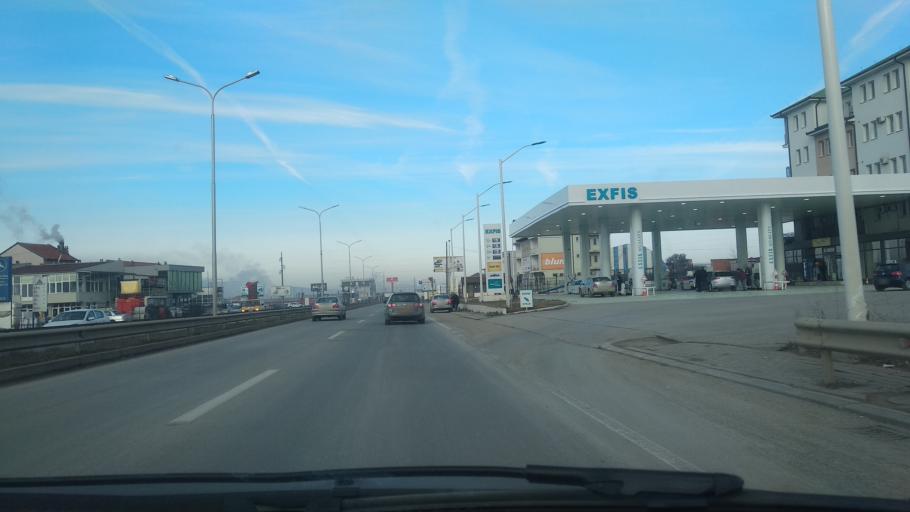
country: XK
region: Pristina
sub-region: Komuna e Prishtines
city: Pristina
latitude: 42.6590
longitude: 21.1350
